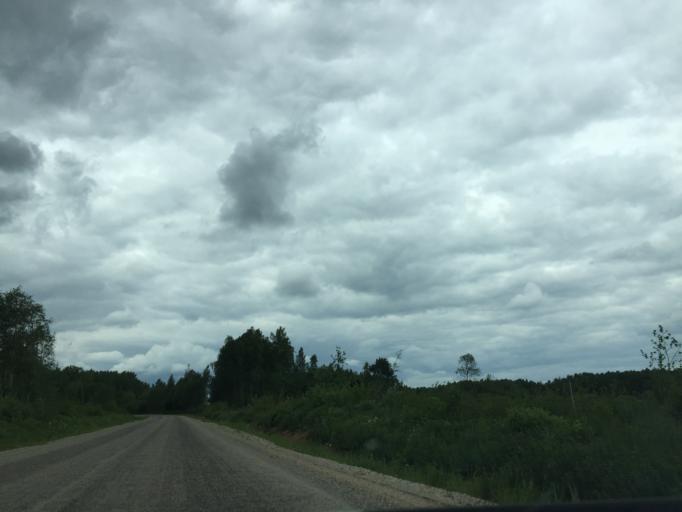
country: LV
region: Dagda
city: Dagda
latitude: 56.0667
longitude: 27.5603
